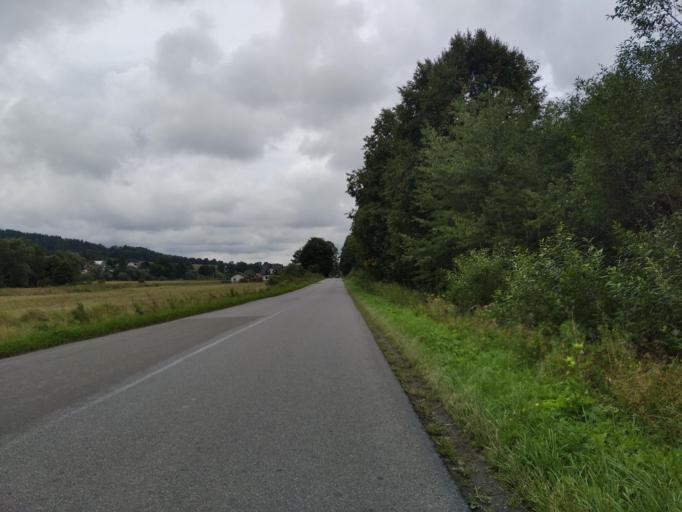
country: PL
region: Subcarpathian Voivodeship
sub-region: Powiat przemyski
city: Bircza
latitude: 49.6839
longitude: 22.4032
